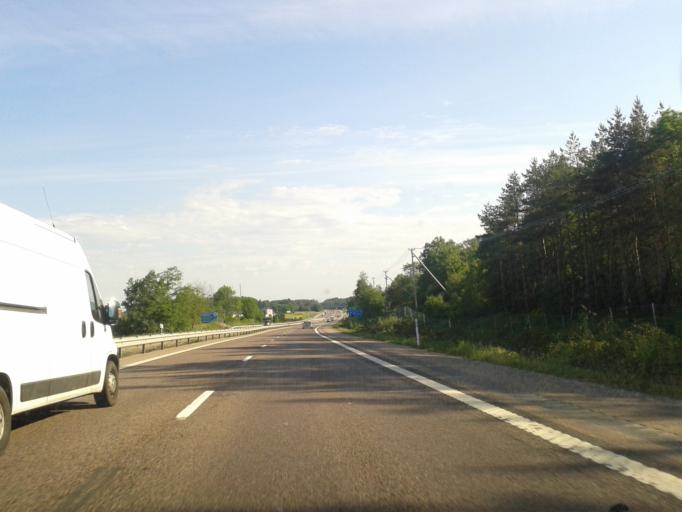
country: SE
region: Vaestra Goetaland
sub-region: Kungalvs Kommun
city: Kode
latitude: 57.9734
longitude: 11.8397
